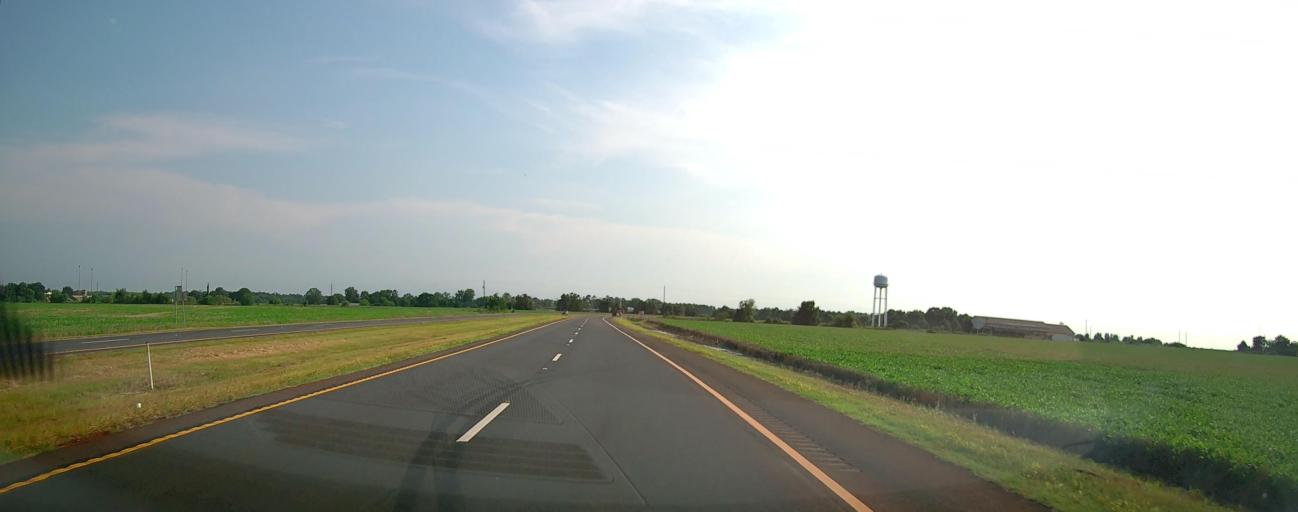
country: US
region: Georgia
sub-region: Peach County
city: Fort Valley
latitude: 32.5749
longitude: -83.9102
